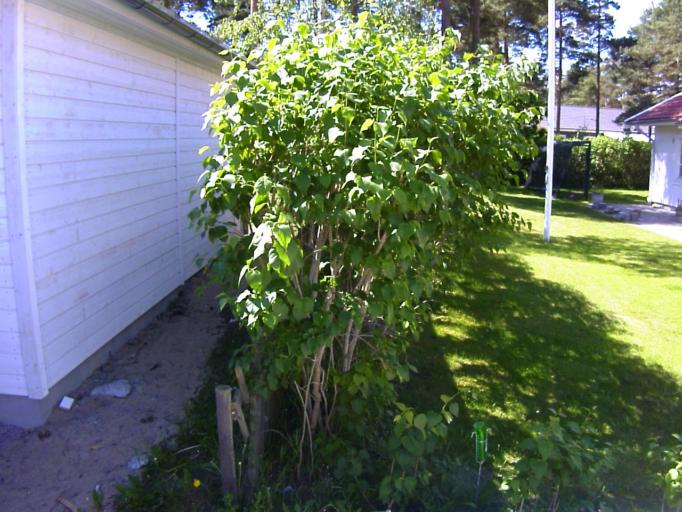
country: SE
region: Skane
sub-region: Kristianstads Kommun
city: Ahus
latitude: 55.9413
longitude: 14.3058
